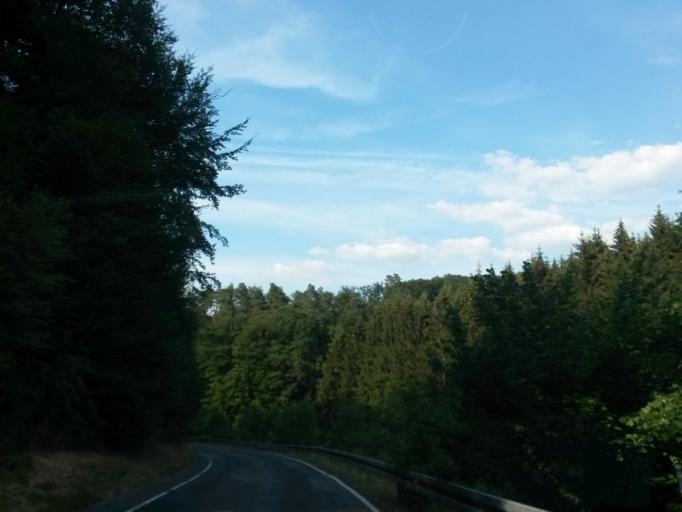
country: DE
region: North Rhine-Westphalia
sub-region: Regierungsbezirk Koln
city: Overath
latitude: 50.9507
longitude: 7.3320
